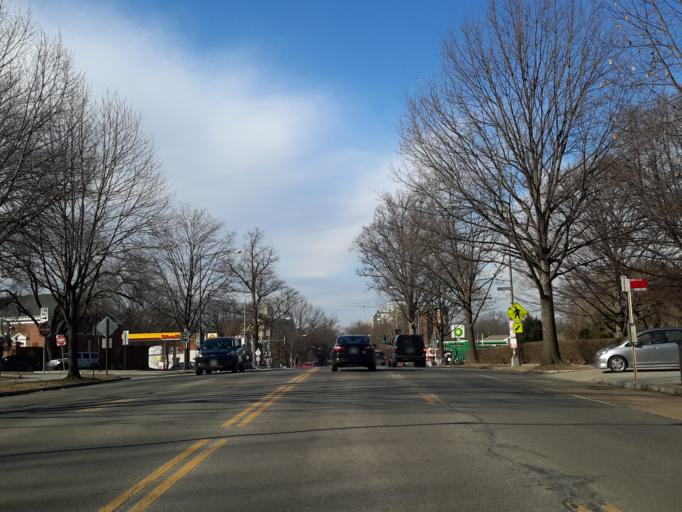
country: US
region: Maryland
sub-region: Montgomery County
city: Chevy Chase Village
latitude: 38.9536
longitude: -77.0690
